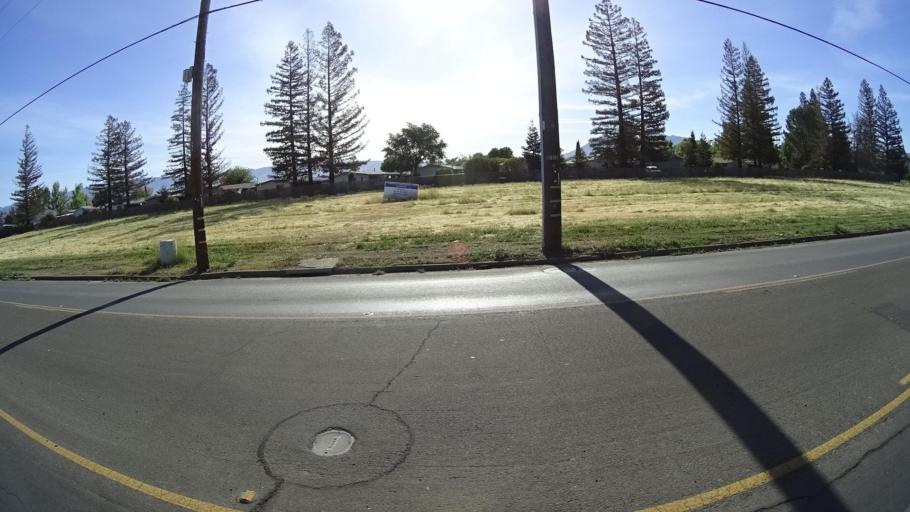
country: US
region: California
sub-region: Lake County
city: Lakeport
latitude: 39.0276
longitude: -122.9163
